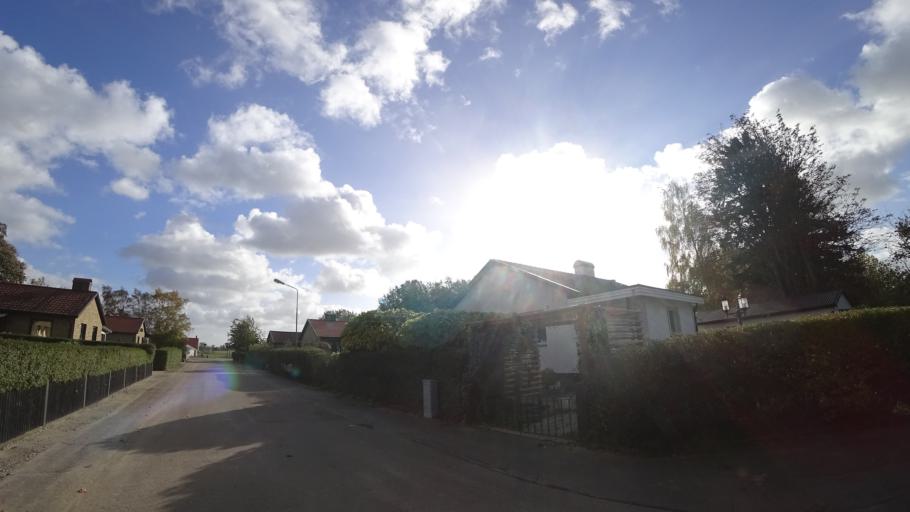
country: SE
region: Skane
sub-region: Staffanstorps Kommun
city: Hjaerup
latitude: 55.6259
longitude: 13.1256
